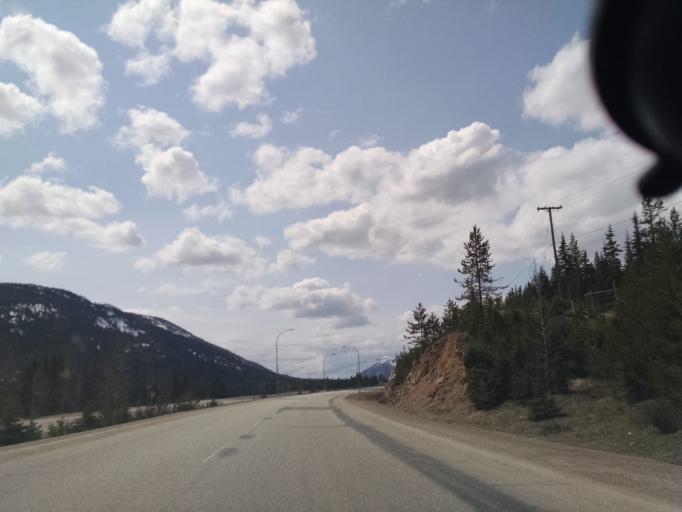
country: CA
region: British Columbia
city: Hope
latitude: 49.6352
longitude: -121.0085
